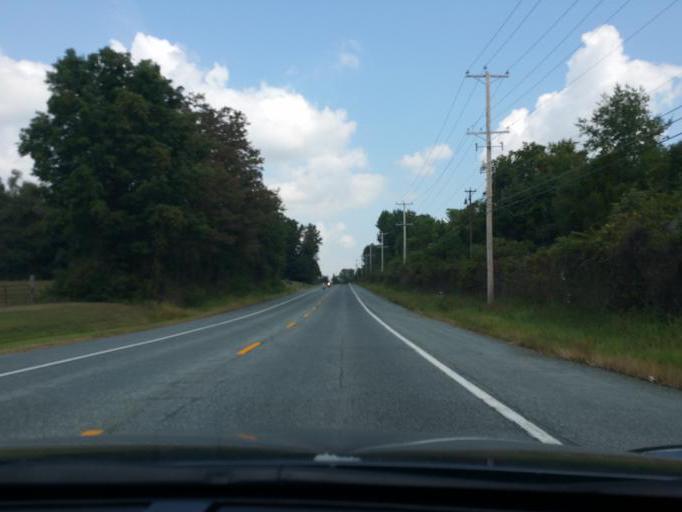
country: US
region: Maryland
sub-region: Cecil County
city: Perryville
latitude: 39.6215
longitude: -76.0942
